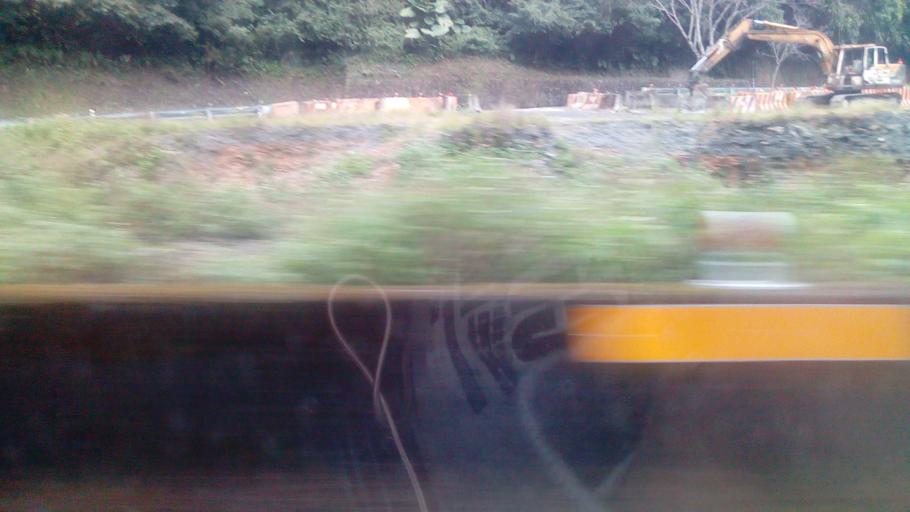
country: TW
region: Taiwan
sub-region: Yilan
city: Yilan
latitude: 24.5836
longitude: 121.4987
